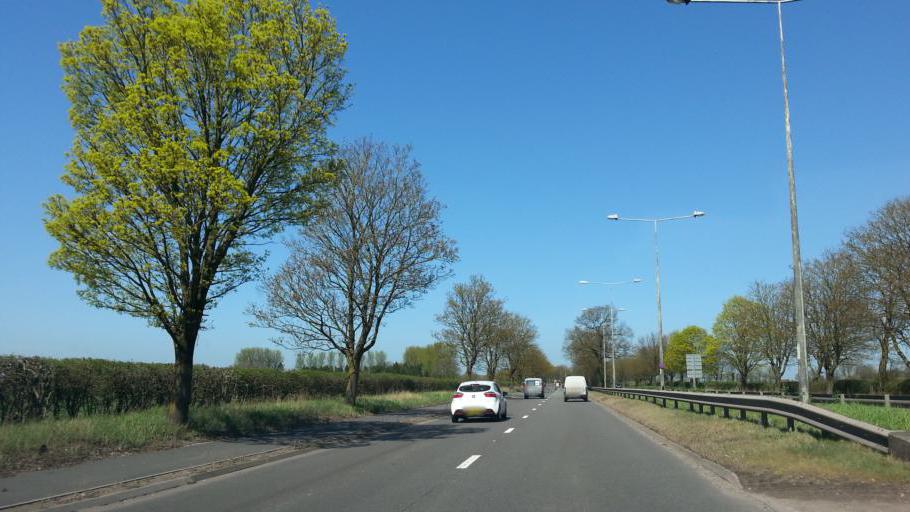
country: GB
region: England
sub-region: Staffordshire
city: Brewood
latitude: 52.6751
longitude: -2.1305
